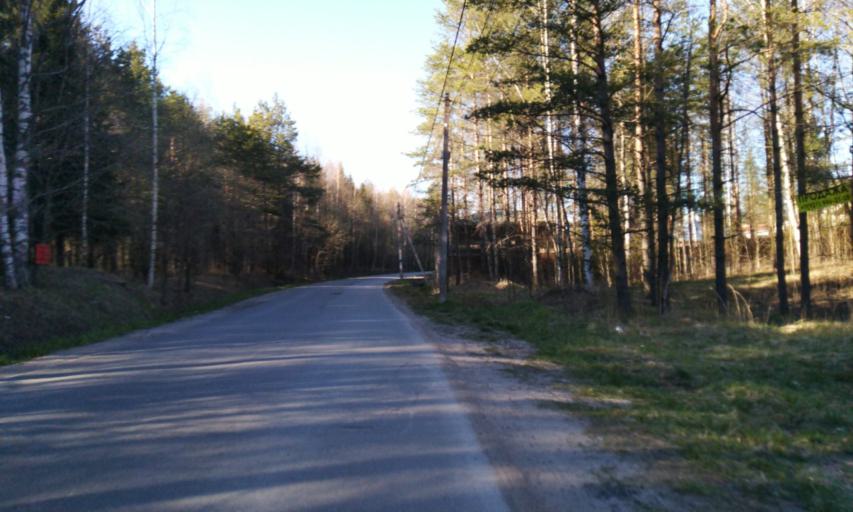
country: RU
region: Leningrad
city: Toksovo
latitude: 60.1399
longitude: 30.5533
